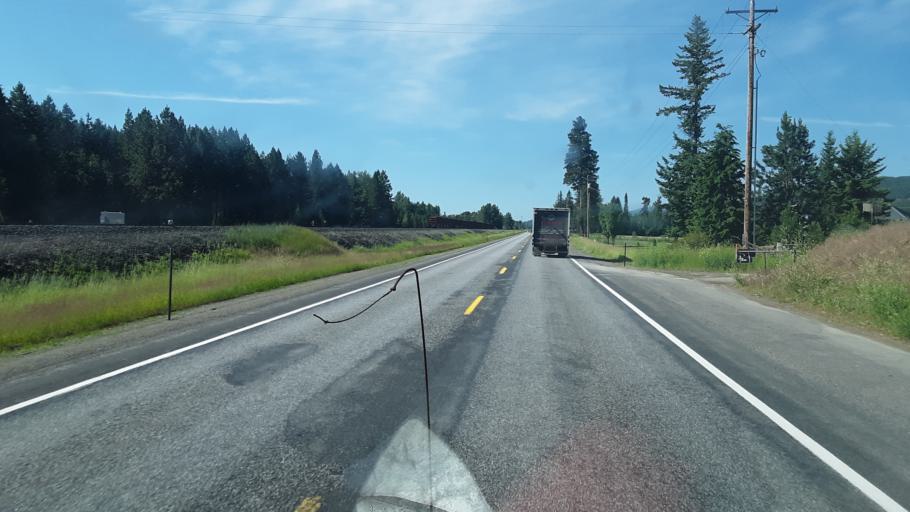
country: US
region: Idaho
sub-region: Bonner County
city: Ponderay
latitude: 48.4803
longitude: -116.4630
